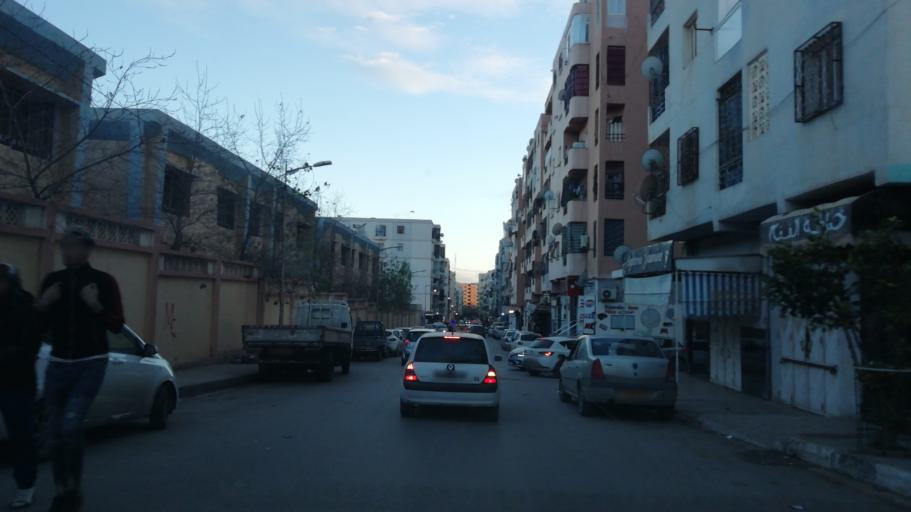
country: DZ
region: Oran
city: Bir el Djir
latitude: 35.7052
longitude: -0.5597
